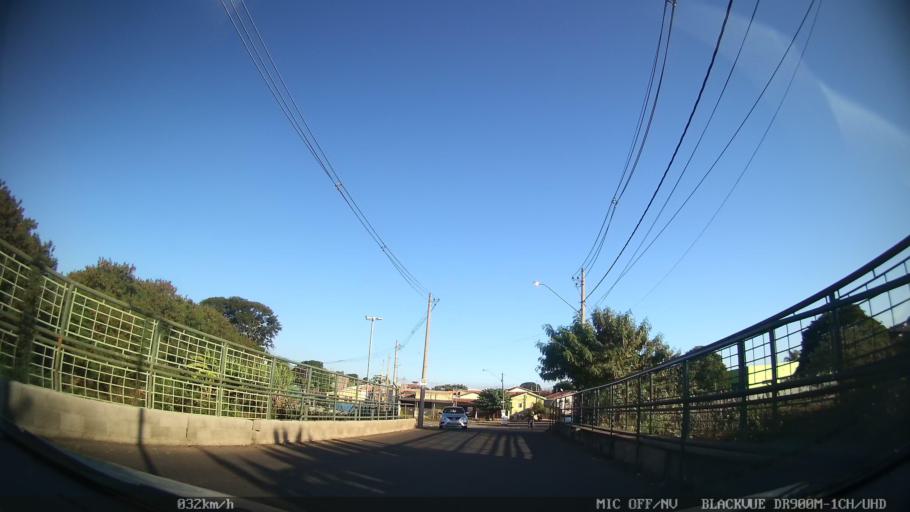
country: BR
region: Sao Paulo
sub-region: Nova Odessa
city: Nova Odessa
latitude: -22.7840
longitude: -47.2835
